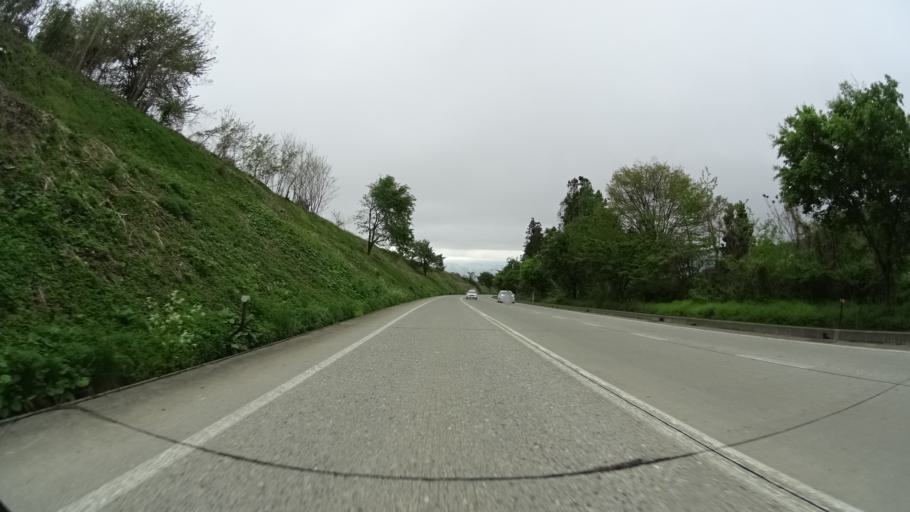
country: JP
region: Nagano
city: Nakano
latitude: 36.7310
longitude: 138.4222
